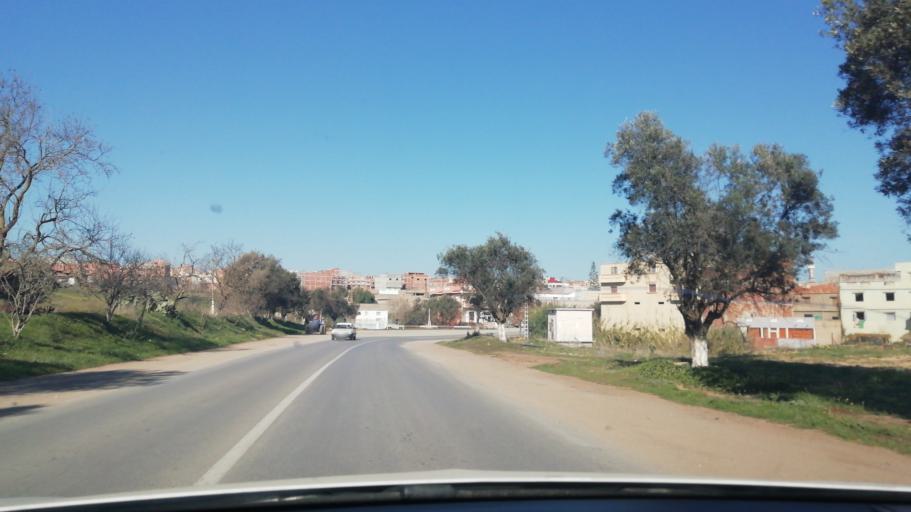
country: DZ
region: Tlemcen
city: Nedroma
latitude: 35.0356
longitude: -1.8936
